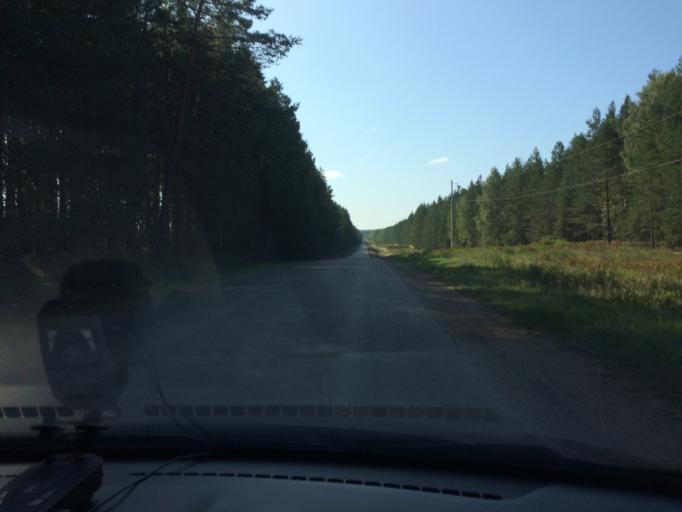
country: RU
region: Mariy-El
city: Sovetskiy
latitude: 56.5720
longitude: 48.4303
